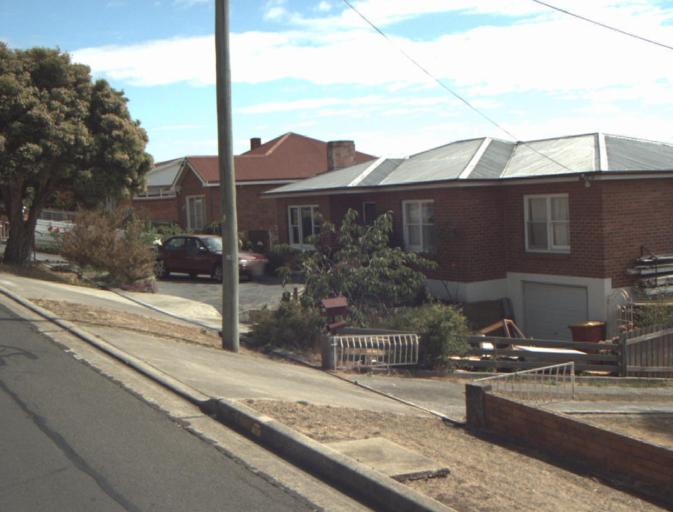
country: AU
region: Tasmania
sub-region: Launceston
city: Summerhill
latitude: -41.4648
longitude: 147.1401
